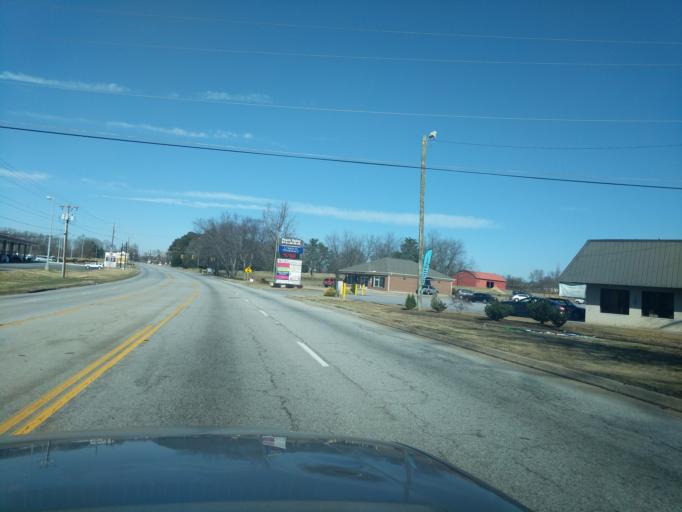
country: US
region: South Carolina
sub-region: Spartanburg County
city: Mayo
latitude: 35.0245
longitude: -81.8953
